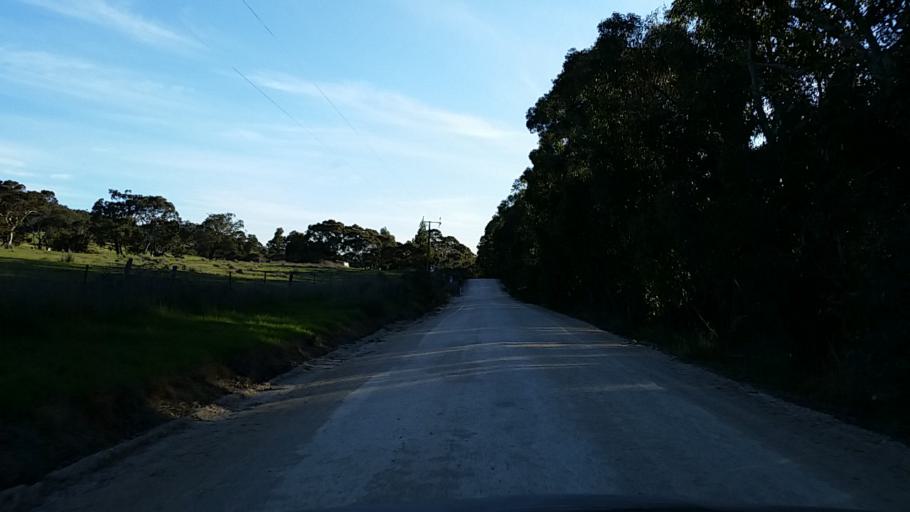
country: AU
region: South Australia
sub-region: Alexandrina
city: Mount Compass
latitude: -35.2949
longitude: 138.6862
